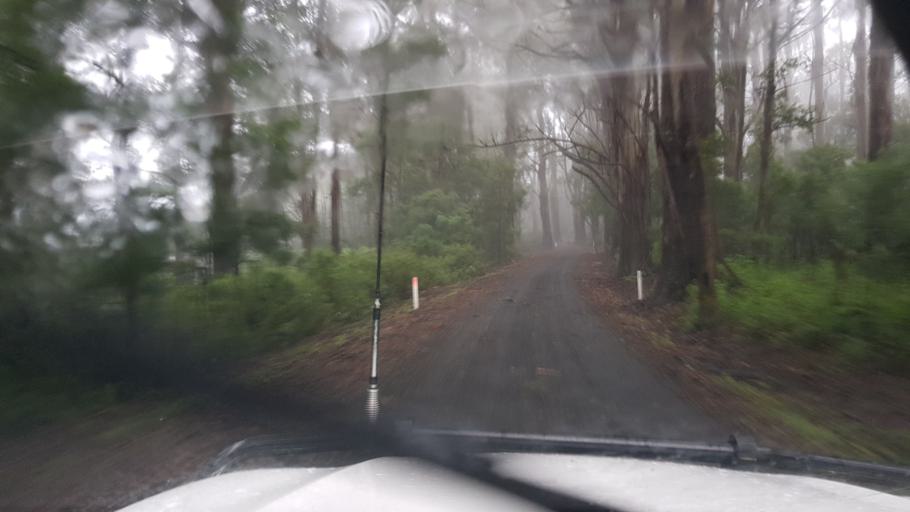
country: AU
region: Victoria
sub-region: Baw Baw
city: Warragul
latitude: -38.2627
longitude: 146.0818
